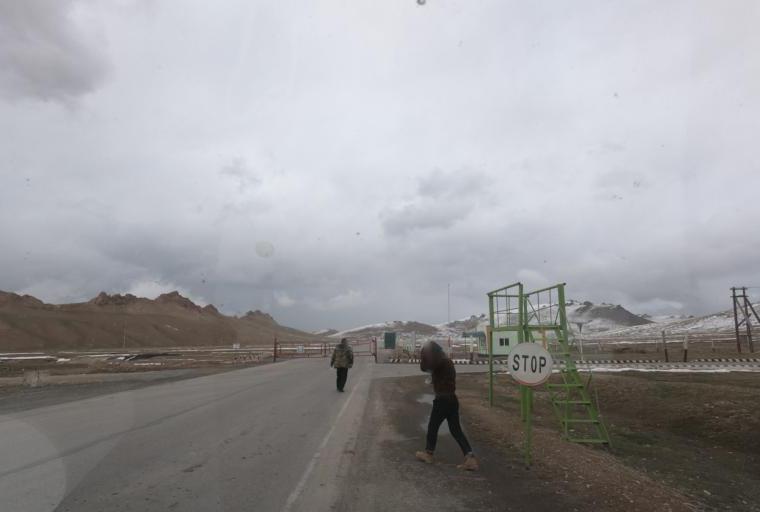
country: KG
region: Naryn
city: Baetov
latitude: 40.7623
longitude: 75.0936
